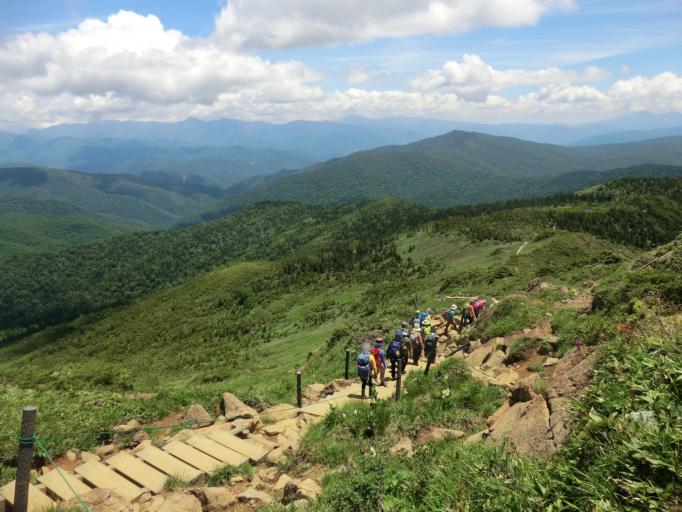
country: JP
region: Gunma
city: Numata
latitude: 36.8953
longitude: 139.1719
